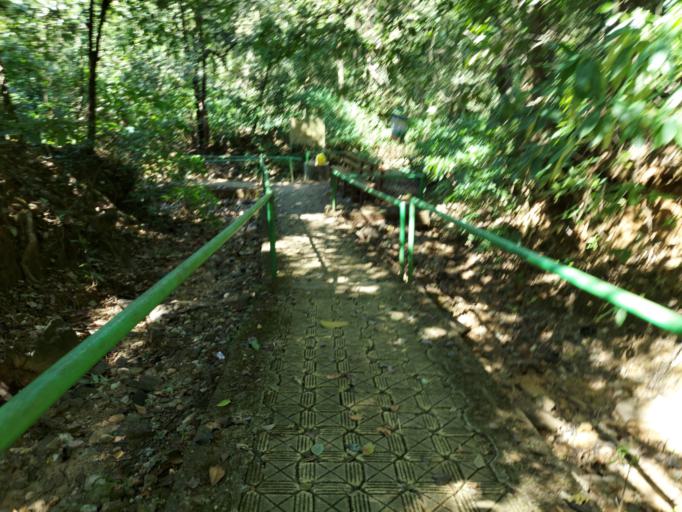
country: IN
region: Maharashtra
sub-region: Sindhudurg
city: Kudal
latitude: 16.0824
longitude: 73.8283
